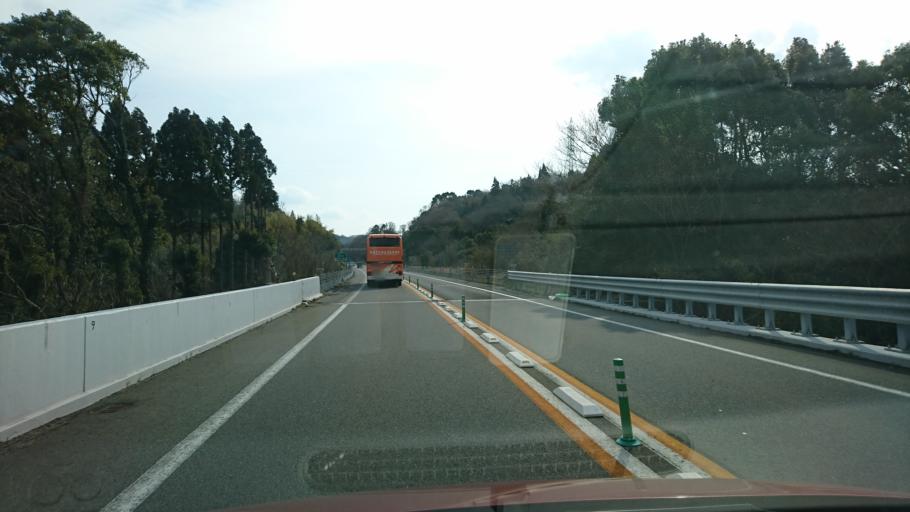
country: JP
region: Hiroshima
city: Innoshima
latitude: 34.2215
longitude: 133.0486
